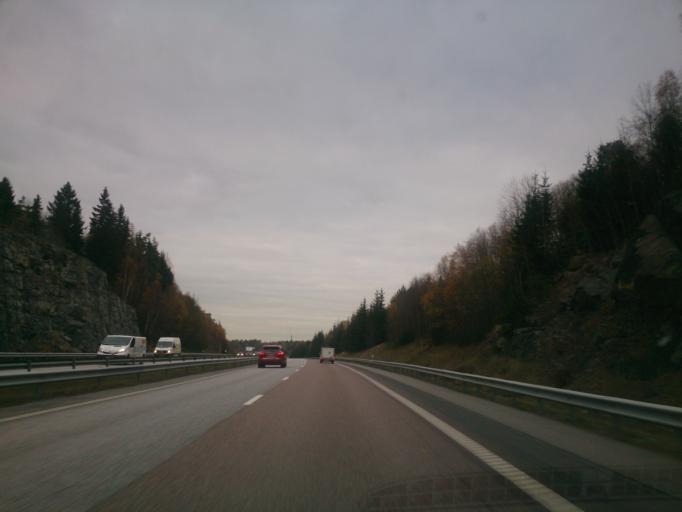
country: SE
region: Stockholm
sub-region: Sodertalje Kommun
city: Pershagen
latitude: 59.1341
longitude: 17.6455
